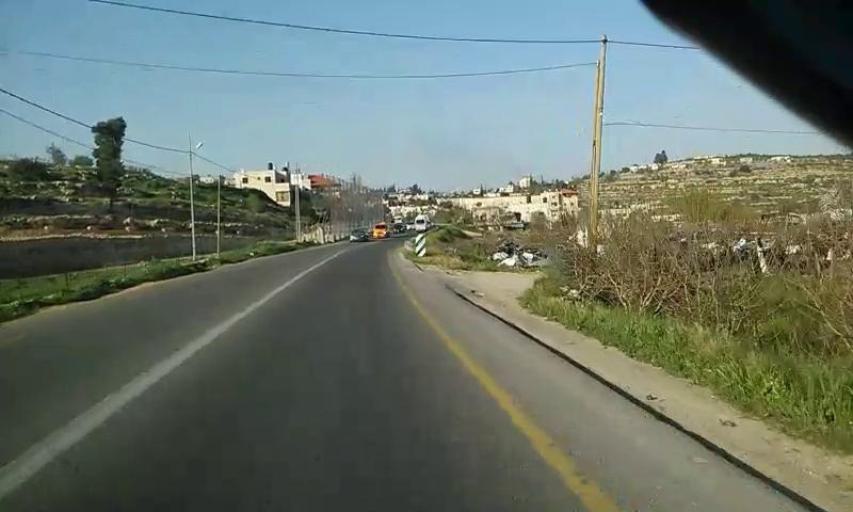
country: PS
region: West Bank
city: Bayt Ummar
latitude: 31.6142
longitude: 35.1139
